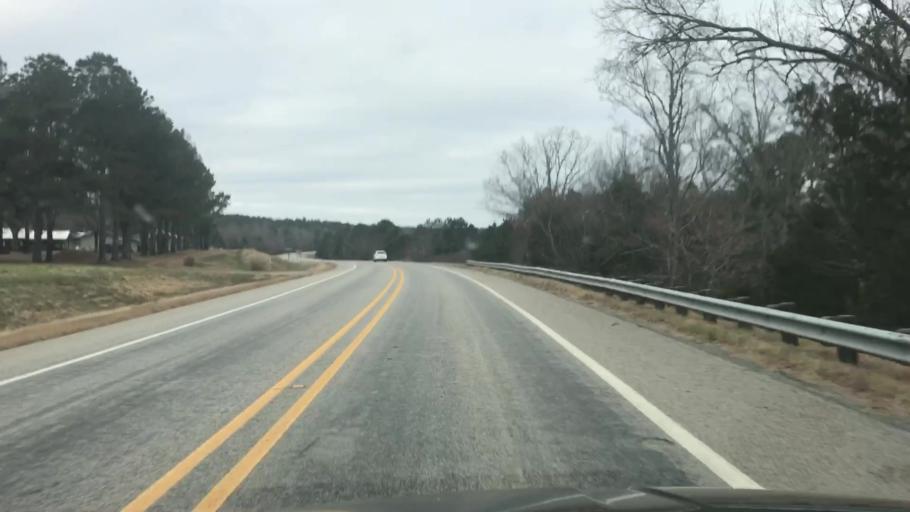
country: US
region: Arkansas
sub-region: Scott County
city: Waldron
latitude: 34.7030
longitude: -93.9208
